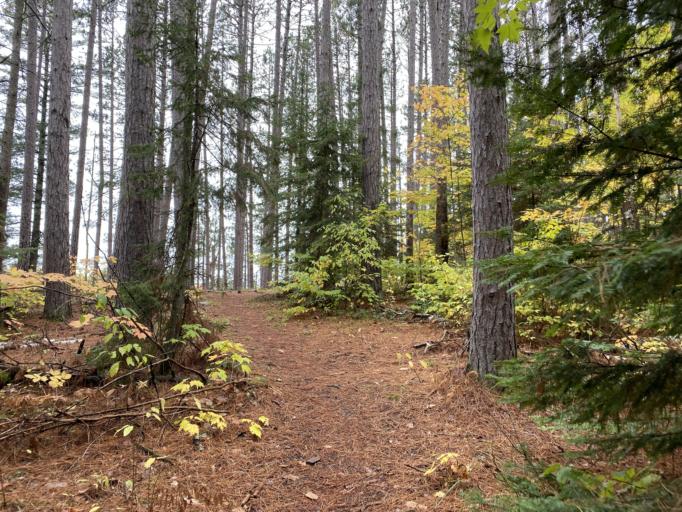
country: US
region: Michigan
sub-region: Marquette County
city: West Ishpeming
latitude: 46.5328
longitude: -88.0014
